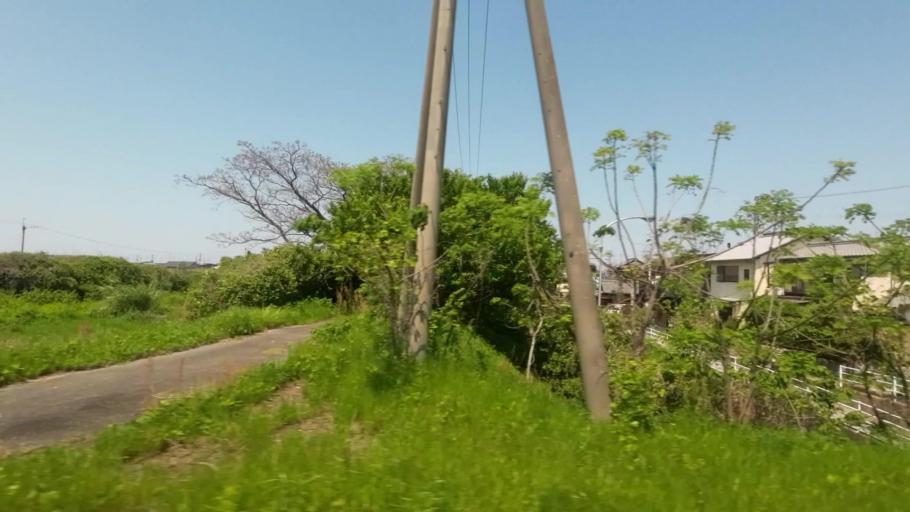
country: JP
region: Ehime
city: Hojo
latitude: 33.9376
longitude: 132.7681
